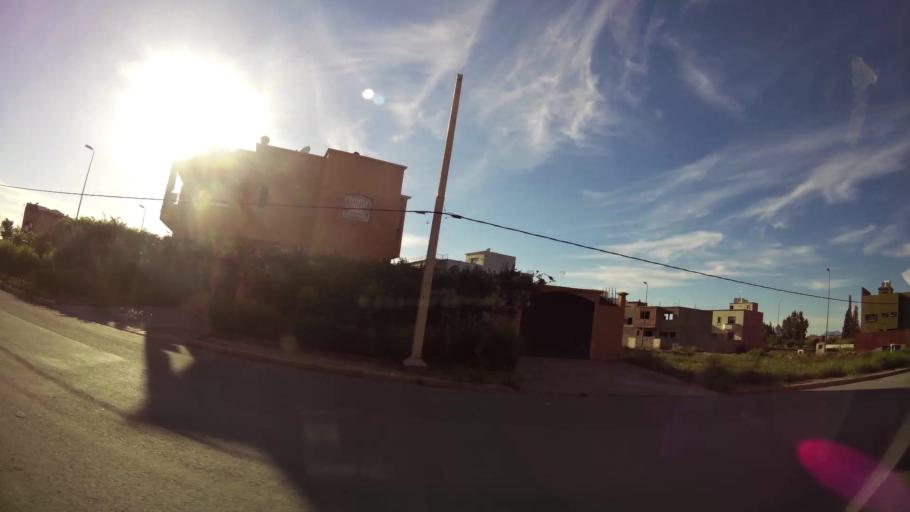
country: MA
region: Marrakech-Tensift-Al Haouz
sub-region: Marrakech
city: Marrakesh
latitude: 31.6778
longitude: -8.0661
